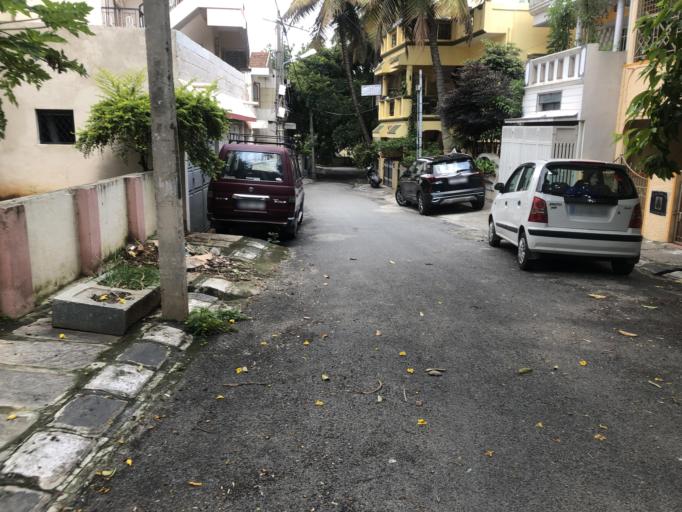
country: IN
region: Karnataka
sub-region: Bangalore Urban
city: Bangalore
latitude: 12.9354
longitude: 77.5490
